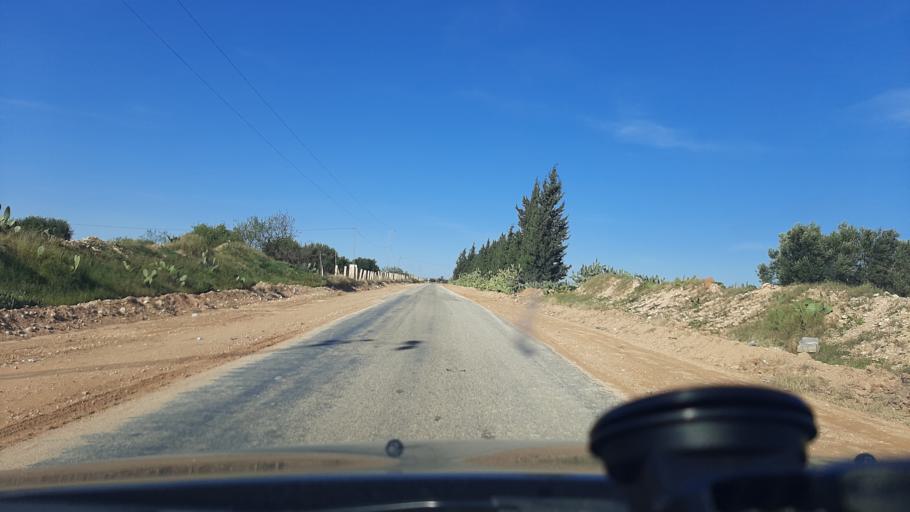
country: TN
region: Safaqis
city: Sfax
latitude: 34.9136
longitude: 10.5870
